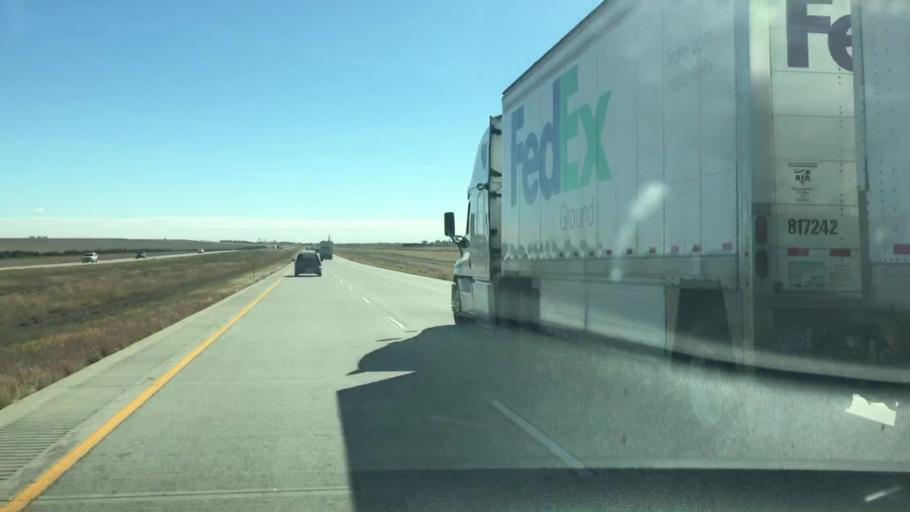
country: US
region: Colorado
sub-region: Lincoln County
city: Limon
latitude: 39.2795
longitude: -103.7637
